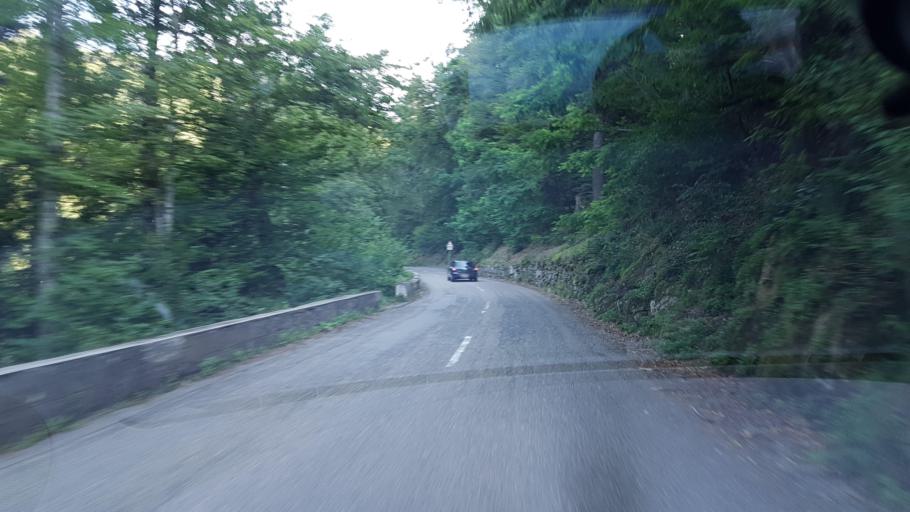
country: DE
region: Baden-Wuerttemberg
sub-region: Freiburg Region
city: Gorwihl
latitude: 47.6287
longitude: 8.0935
